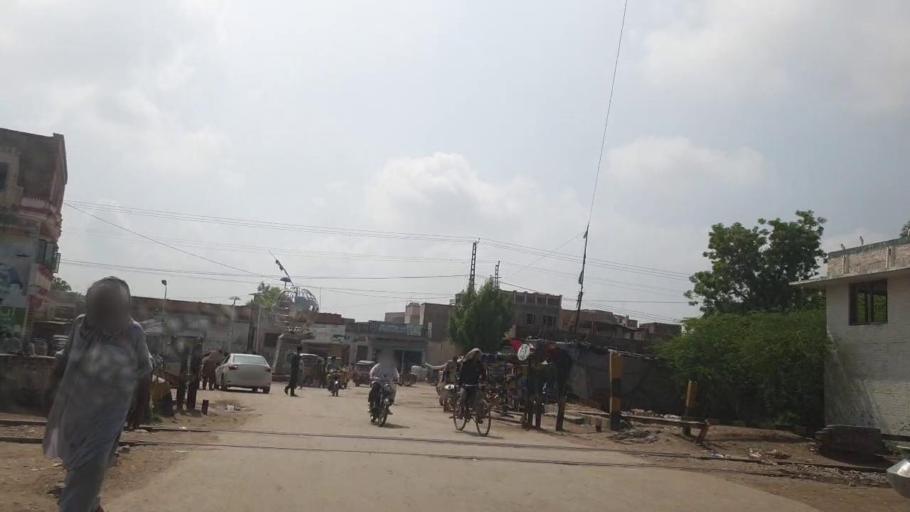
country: PK
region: Sindh
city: Khairpur
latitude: 27.5232
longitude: 68.7406
